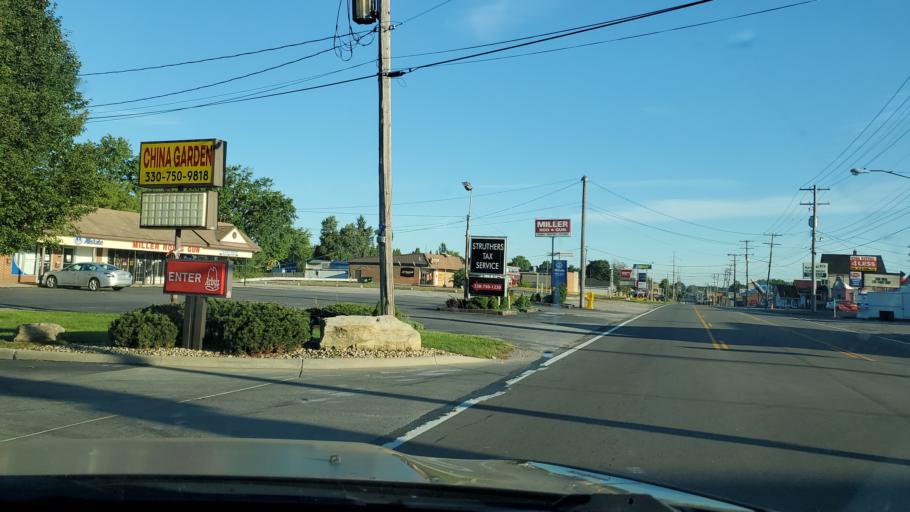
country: US
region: Ohio
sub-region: Mahoning County
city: Struthers
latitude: 41.0470
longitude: -80.6158
